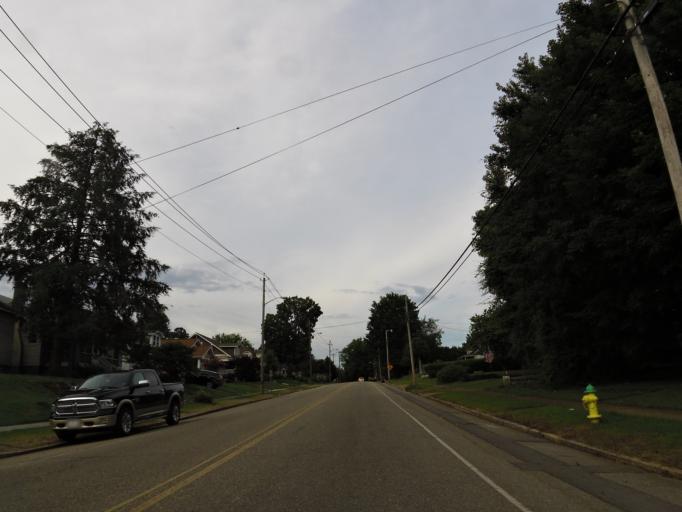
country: US
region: Tennessee
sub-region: Knox County
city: Knoxville
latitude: 35.9954
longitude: -83.9189
